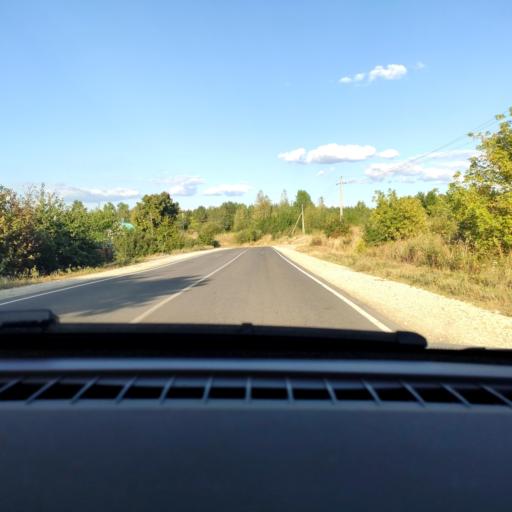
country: RU
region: Voronezj
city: Semiluki
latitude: 51.6608
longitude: 39.0092
